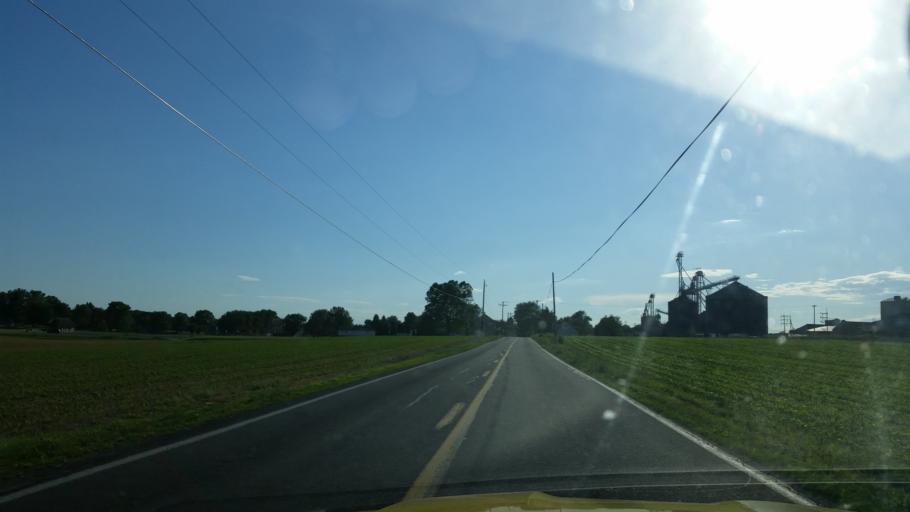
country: US
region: Pennsylvania
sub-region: Lebanon County
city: Avon
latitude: 40.3471
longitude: -76.3785
